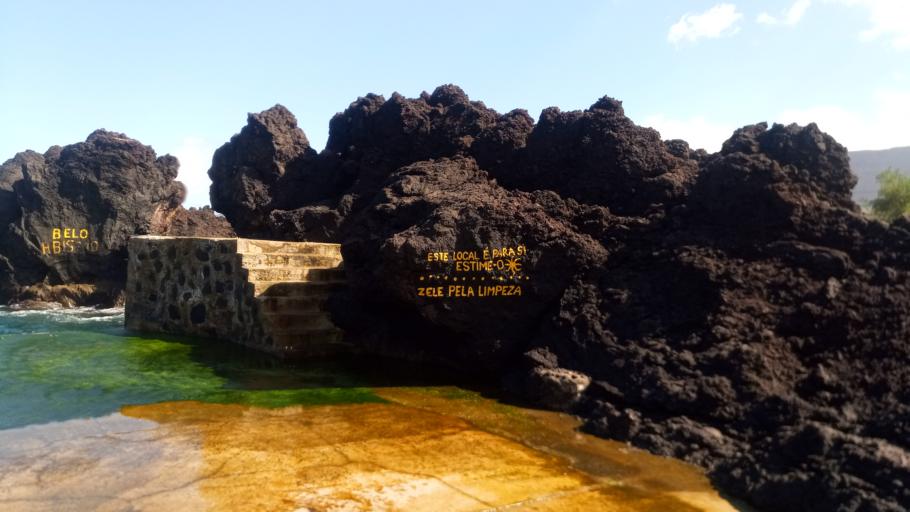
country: PT
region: Azores
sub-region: Praia da Vitoria
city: Biscoitos
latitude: 38.8026
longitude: -27.2565
